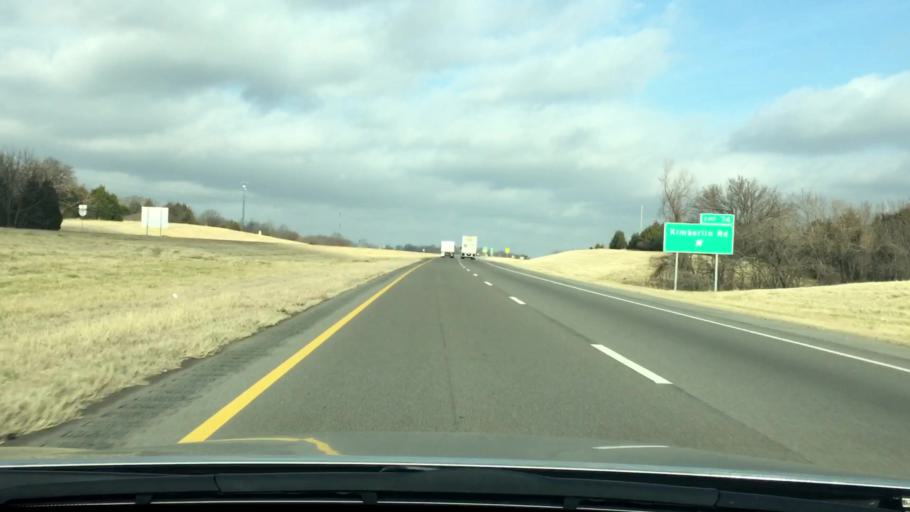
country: US
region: Oklahoma
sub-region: Garvin County
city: Pauls Valley
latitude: 34.7545
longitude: -97.2781
